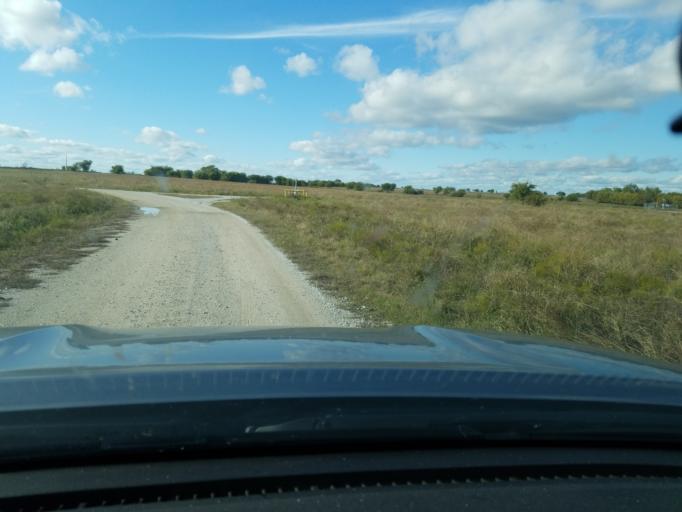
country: US
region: Texas
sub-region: Tarrant County
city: Haslet
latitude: 32.9914
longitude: -97.4113
